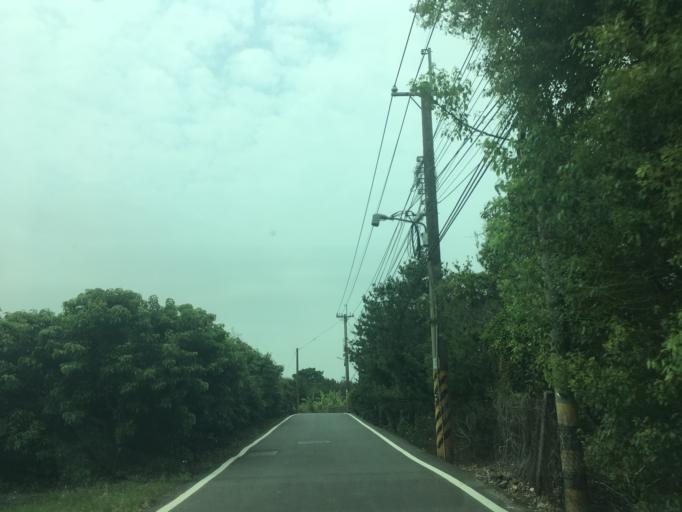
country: TW
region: Taiwan
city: Zhongxing New Village
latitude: 24.0392
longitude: 120.6846
